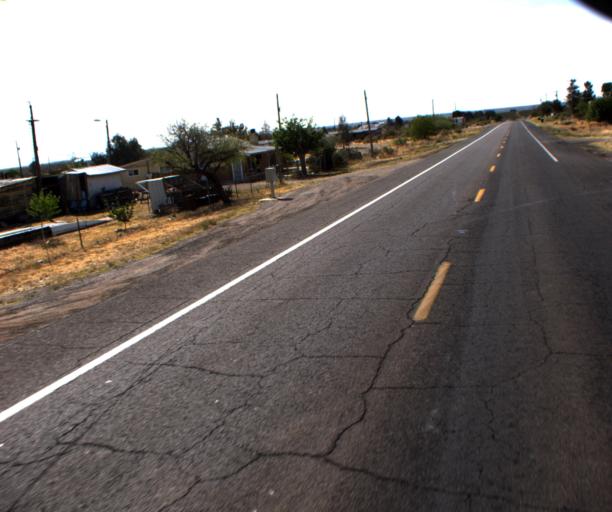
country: US
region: Arizona
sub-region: Graham County
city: Swift Trail Junction
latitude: 32.7256
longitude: -109.7124
